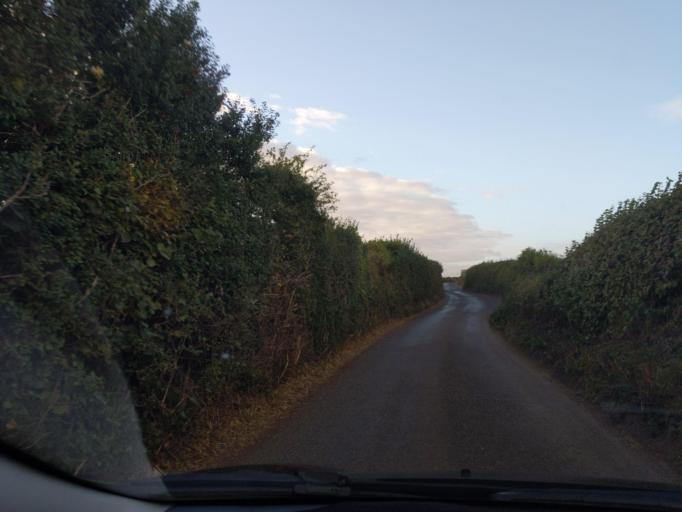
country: GB
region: England
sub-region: Devon
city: Salcombe
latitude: 50.2377
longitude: -3.8209
